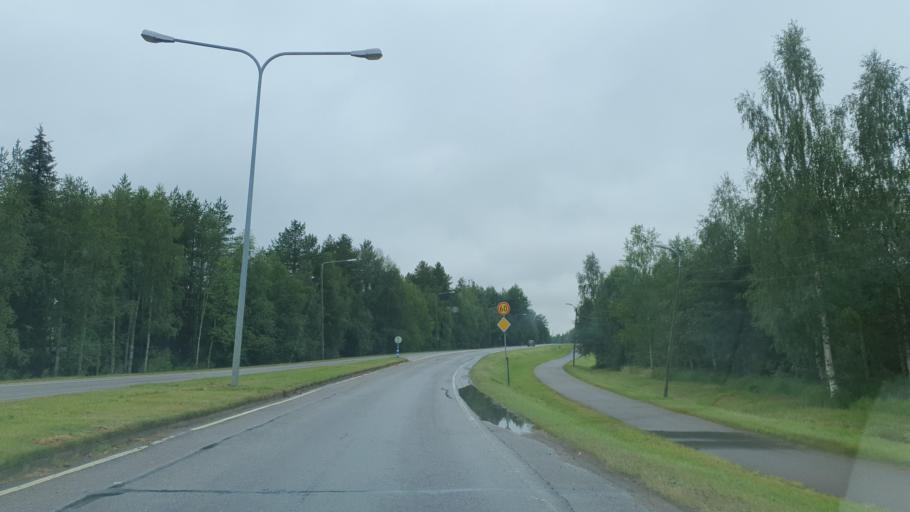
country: FI
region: Lapland
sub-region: Itae-Lappi
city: Kemijaervi
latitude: 66.7185
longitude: 27.3842
